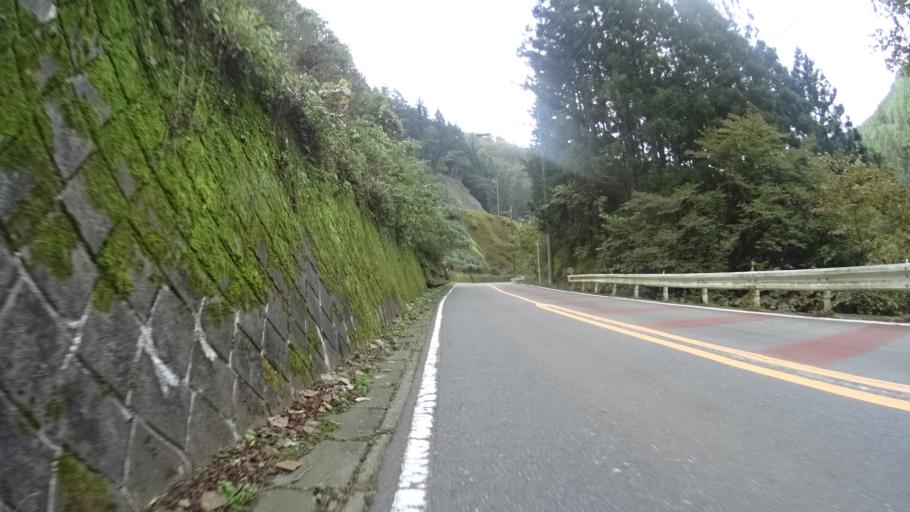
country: JP
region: Yamanashi
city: Uenohara
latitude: 35.6991
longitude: 139.1009
